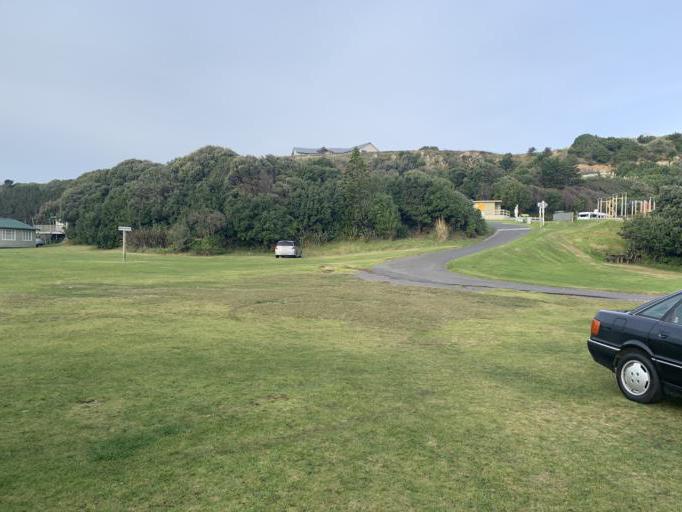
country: NZ
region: Taranaki
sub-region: South Taranaki District
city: Hawera
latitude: -39.5654
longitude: 174.0612
